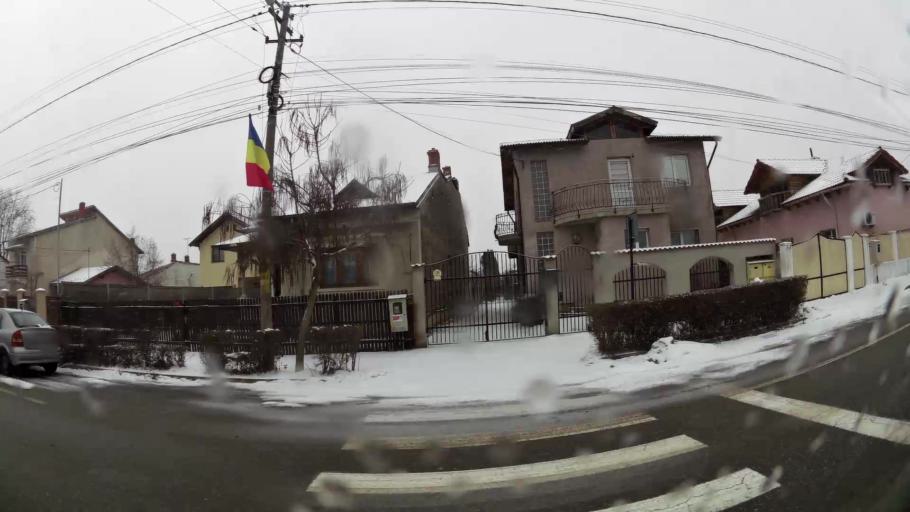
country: RO
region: Dambovita
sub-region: Municipiul Targoviste
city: Targoviste
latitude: 44.9366
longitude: 25.4491
